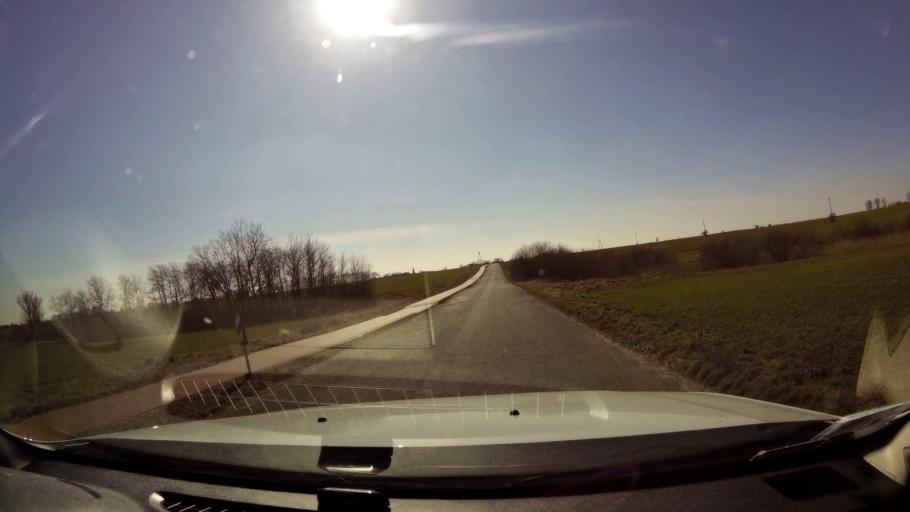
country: PL
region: West Pomeranian Voivodeship
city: Trzcinsko Zdroj
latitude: 52.9809
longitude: 14.6073
